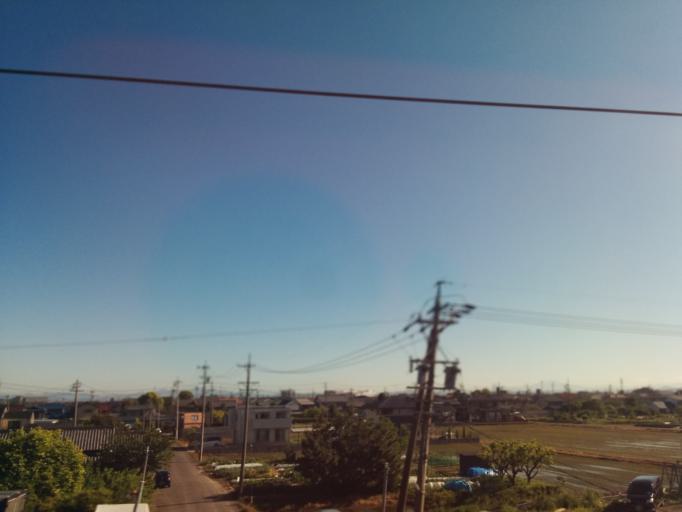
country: JP
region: Aichi
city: Inazawa
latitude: 35.2247
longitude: 136.8262
